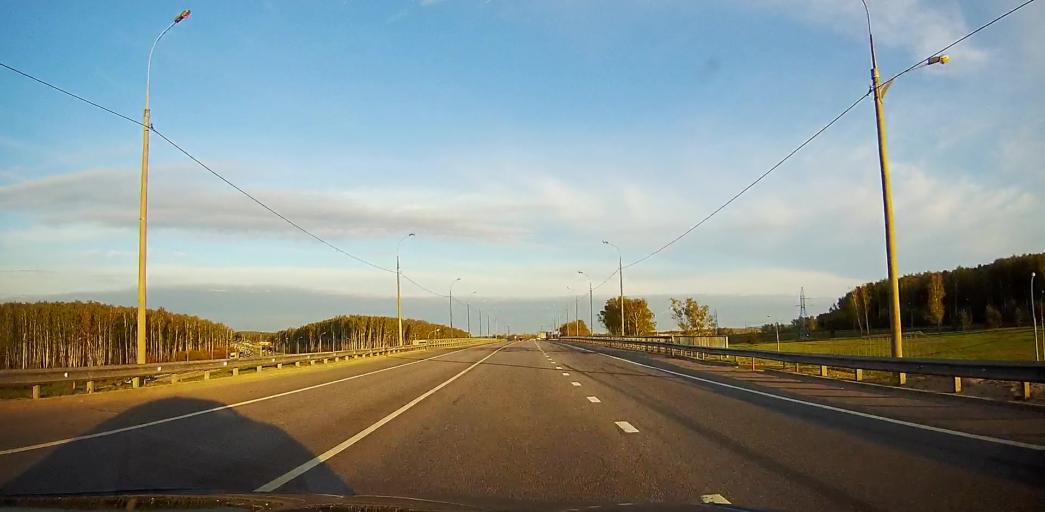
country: RU
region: Moskovskaya
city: Troitskoye
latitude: 55.2364
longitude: 38.5459
